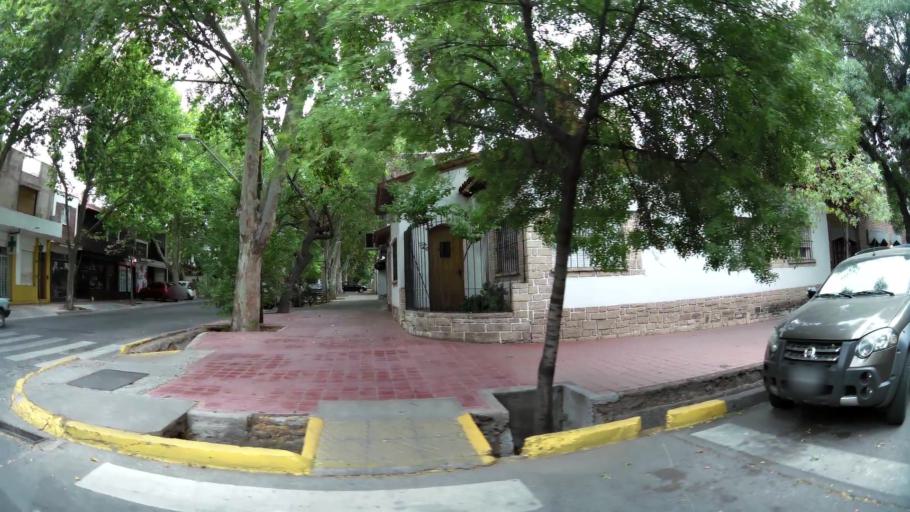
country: AR
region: Mendoza
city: Mendoza
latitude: -32.8900
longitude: -68.8542
